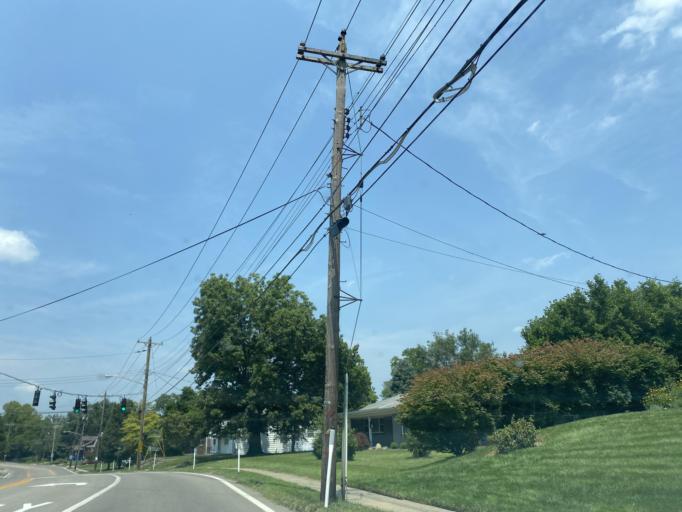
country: US
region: Kentucky
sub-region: Campbell County
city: Fort Thomas
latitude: 39.0559
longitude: -84.4494
